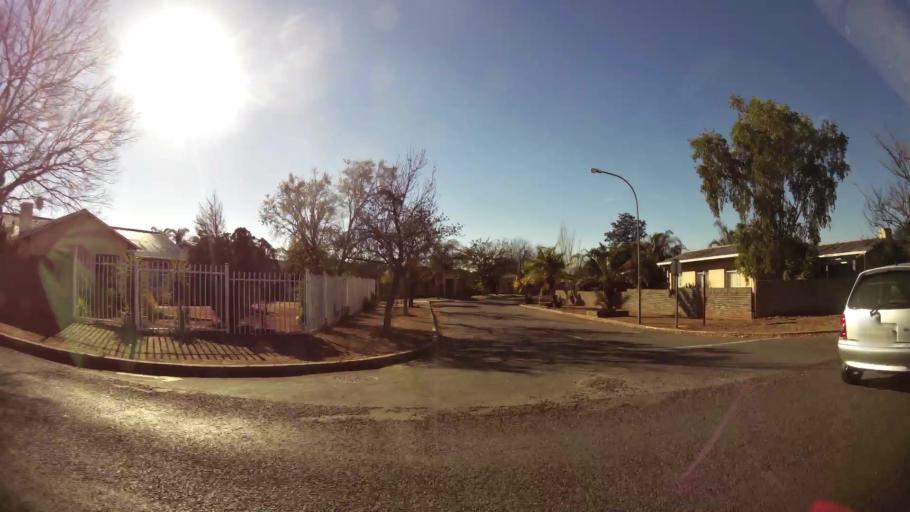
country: ZA
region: Northern Cape
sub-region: Frances Baard District Municipality
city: Kimberley
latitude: -28.7450
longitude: 24.7920
